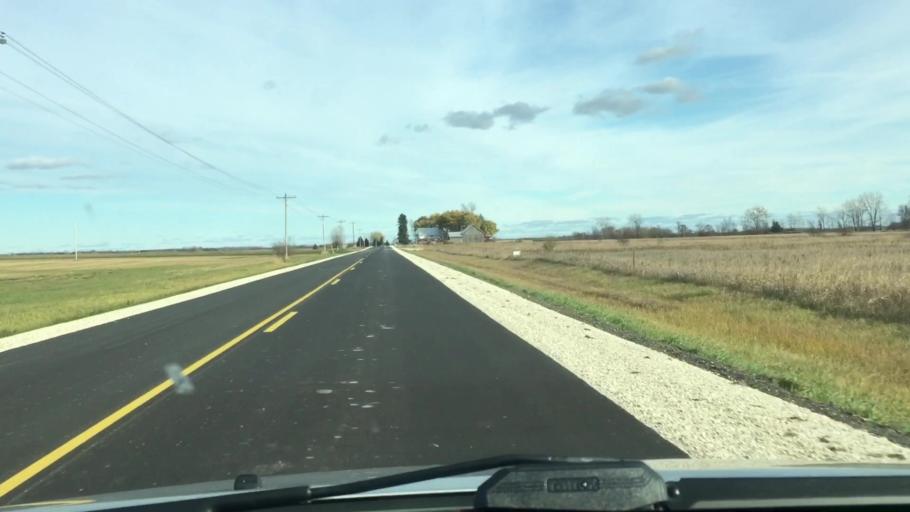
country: US
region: Wisconsin
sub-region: Kewaunee County
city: Algoma
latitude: 44.6897
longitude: -87.5175
